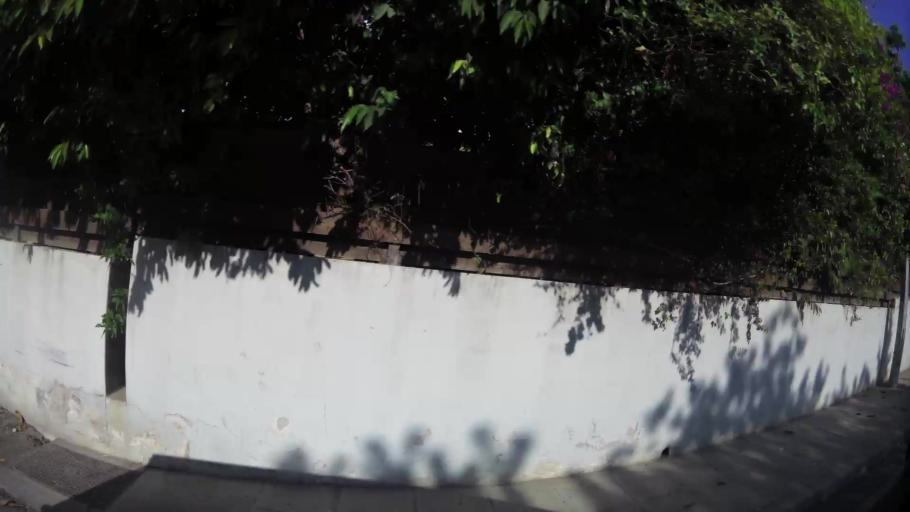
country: CY
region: Lefkosia
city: Nicosia
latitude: 35.1755
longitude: 33.3487
